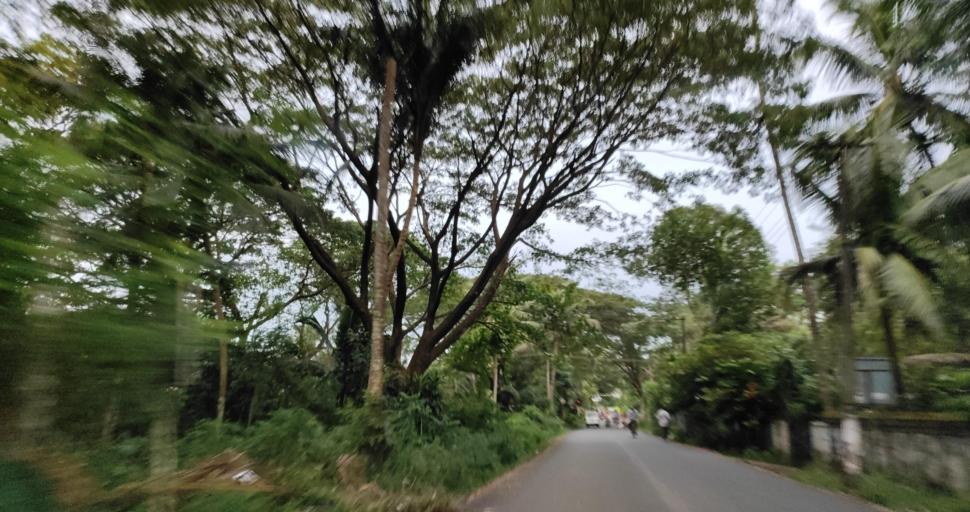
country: IN
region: Kerala
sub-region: Alappuzha
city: Vayalar
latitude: 9.6875
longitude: 76.3291
